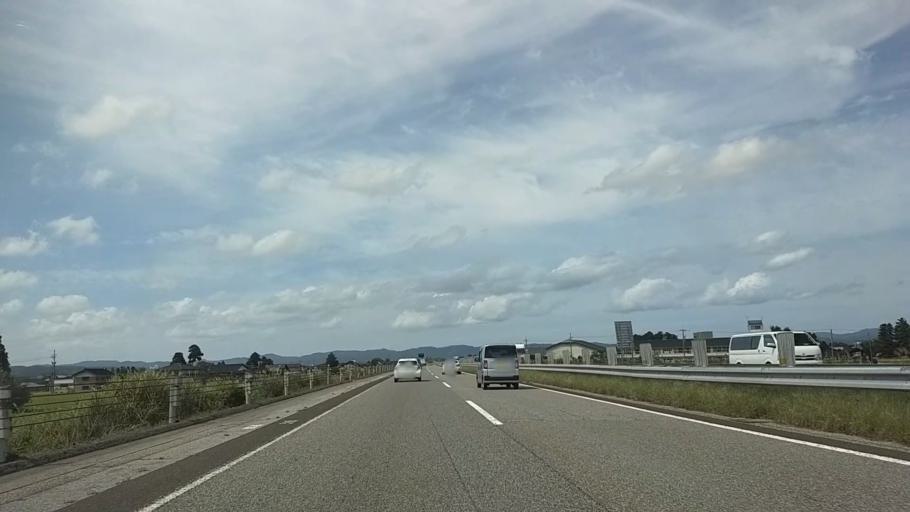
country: JP
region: Toyama
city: Nanto-shi
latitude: 36.6245
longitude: 136.9309
